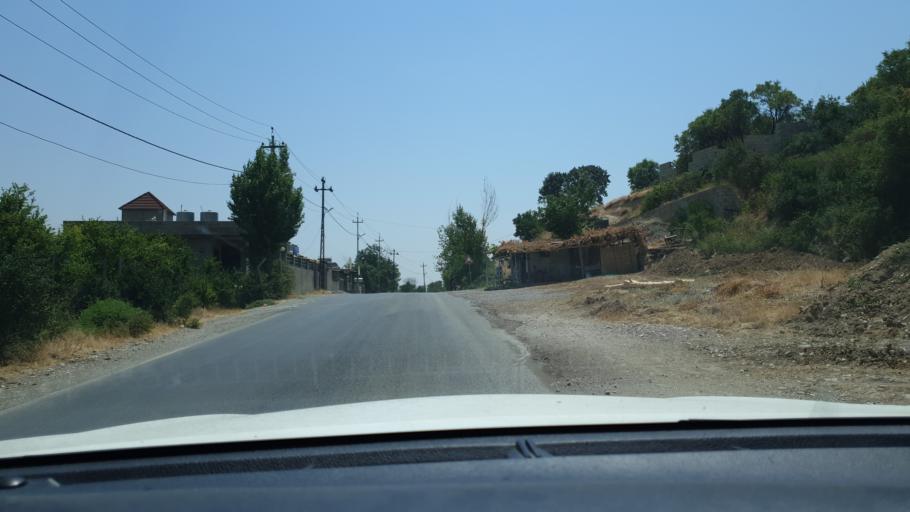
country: IQ
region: Arbil
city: Nahiyat Hiran
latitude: 36.2860
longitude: 44.4869
